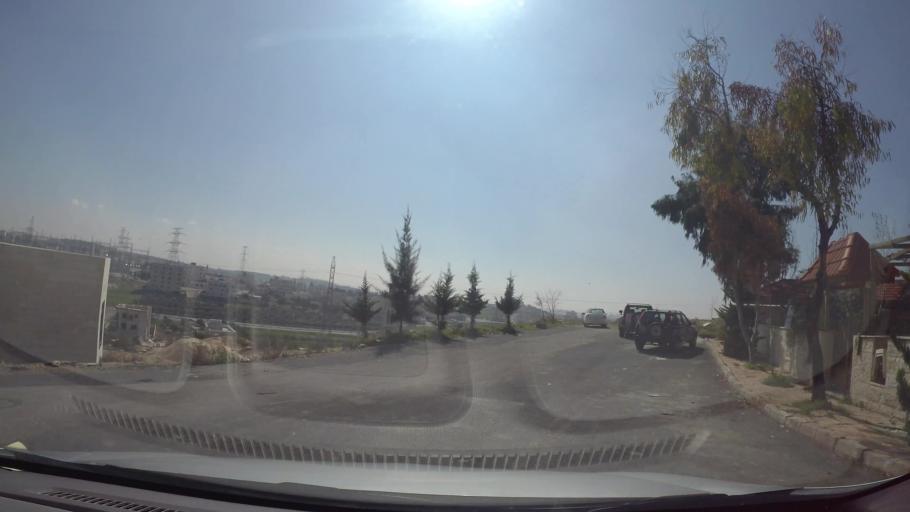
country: JO
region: Amman
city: Al Bunayyat ash Shamaliyah
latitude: 31.8930
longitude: 35.9007
